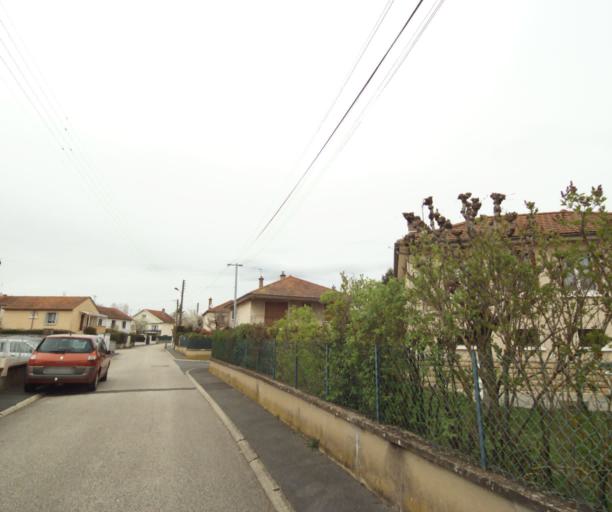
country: FR
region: Bourgogne
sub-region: Departement de Saone-et-Loire
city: Charnay-les-Macon
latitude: 46.3111
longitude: 4.7999
